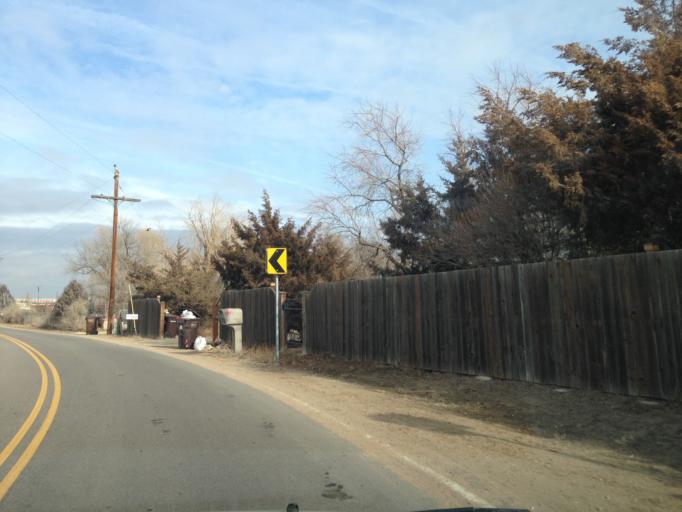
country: US
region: Colorado
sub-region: Boulder County
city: Lafayette
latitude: 39.9981
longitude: -105.0601
